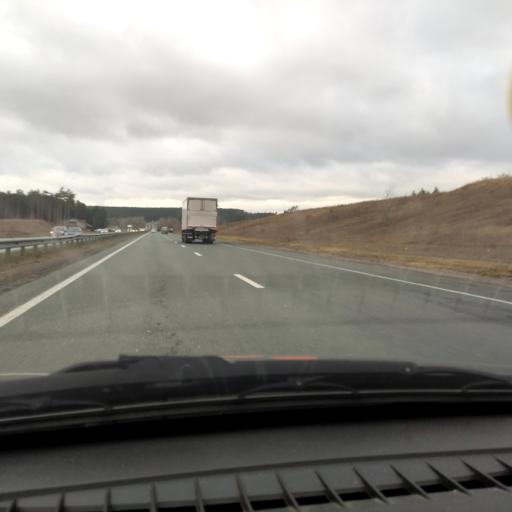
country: RU
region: Samara
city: Zhigulevsk
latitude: 53.5221
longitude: 49.5298
